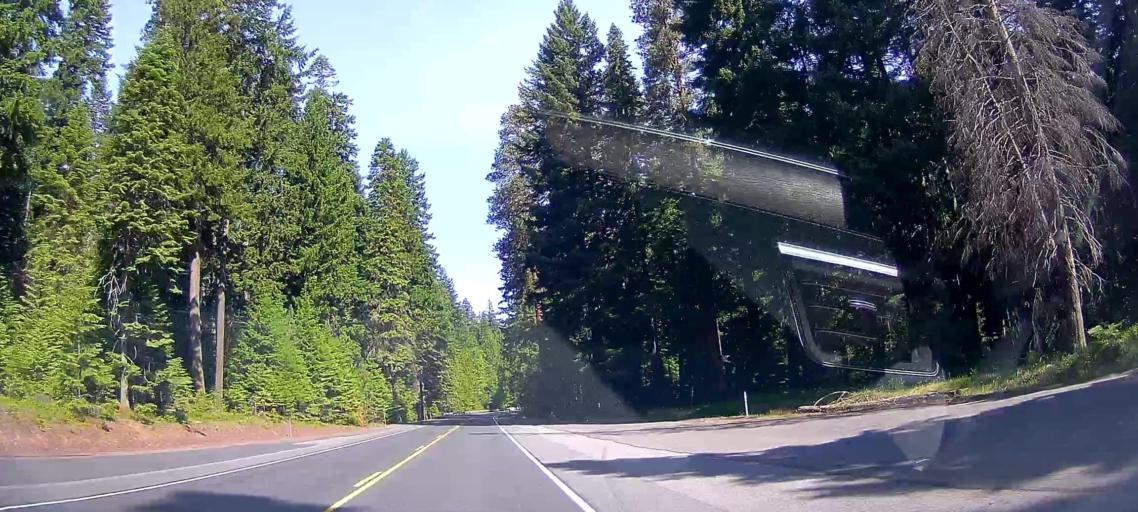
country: US
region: Oregon
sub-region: Jefferson County
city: Warm Springs
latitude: 45.0928
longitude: -121.5508
